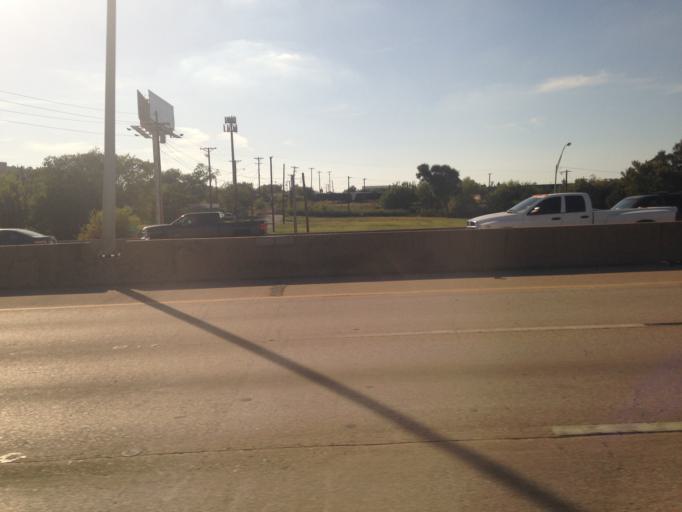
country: US
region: Texas
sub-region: Tarrant County
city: Fort Worth
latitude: 32.7297
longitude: -97.3203
